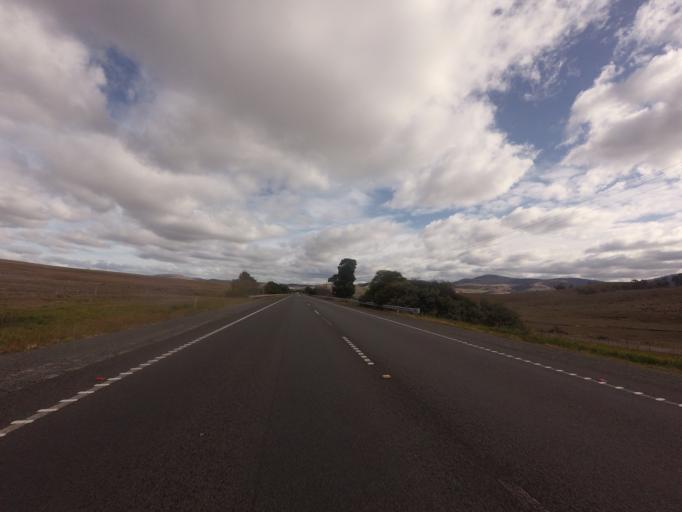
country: AU
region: Tasmania
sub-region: Brighton
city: Bridgewater
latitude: -42.4637
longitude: 147.1881
